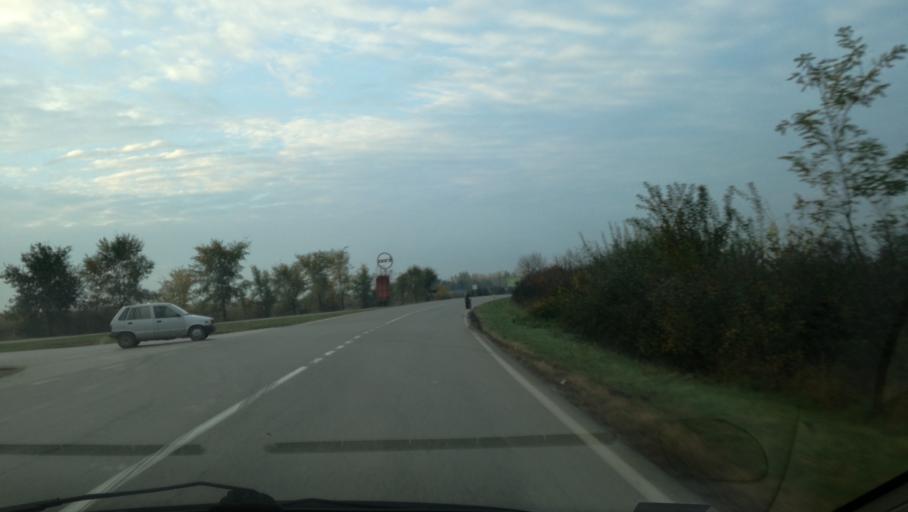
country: RS
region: Autonomna Pokrajina Vojvodina
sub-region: Severnobanatski Okrug
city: Kikinda
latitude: 45.7982
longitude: 20.4395
